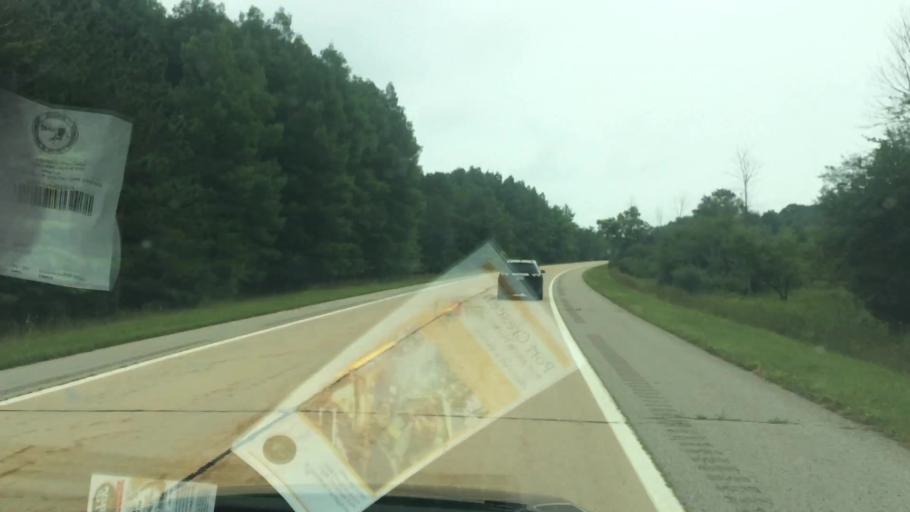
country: US
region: Michigan
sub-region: Huron County
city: Harbor Beach
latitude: 44.0268
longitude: -82.8247
